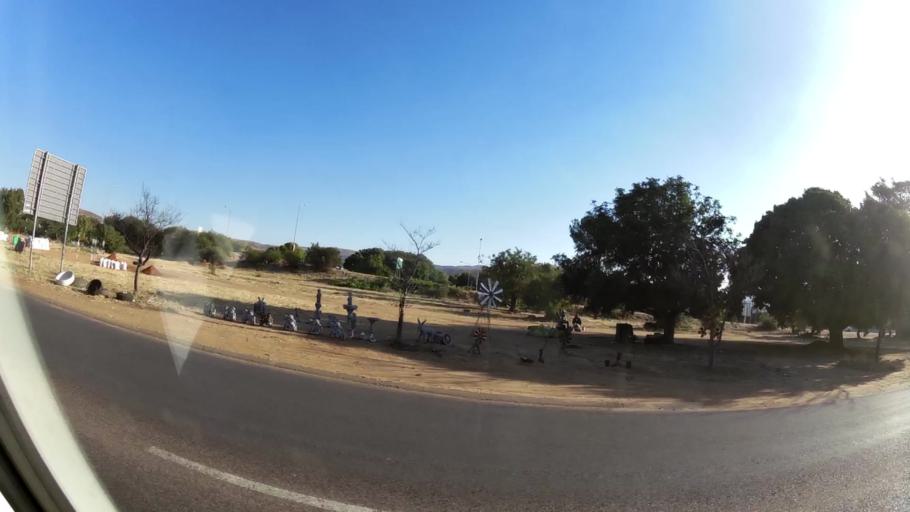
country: ZA
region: North-West
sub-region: Bojanala Platinum District Municipality
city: Rustenburg
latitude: -25.6869
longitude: 27.2263
